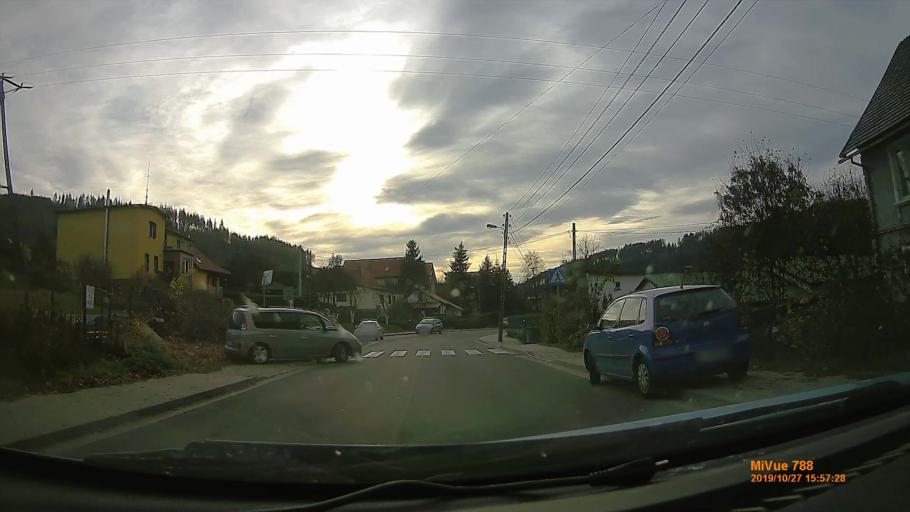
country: PL
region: Lower Silesian Voivodeship
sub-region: Powiat klodzki
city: Bozkow
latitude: 50.5435
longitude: 16.5404
